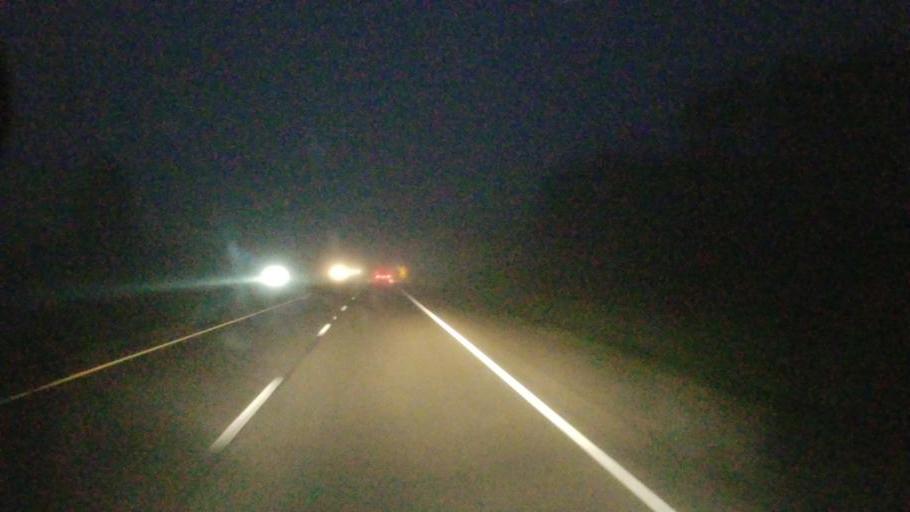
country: US
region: Ohio
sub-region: Ross County
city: Kingston
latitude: 39.4694
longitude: -82.9705
